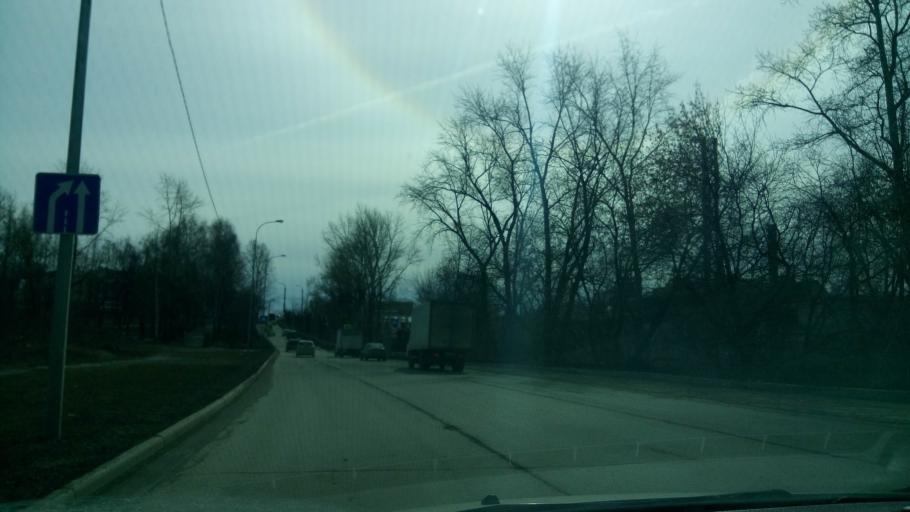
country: RU
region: Sverdlovsk
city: Nizhniy Tagil
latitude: 57.9074
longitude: 59.9464
